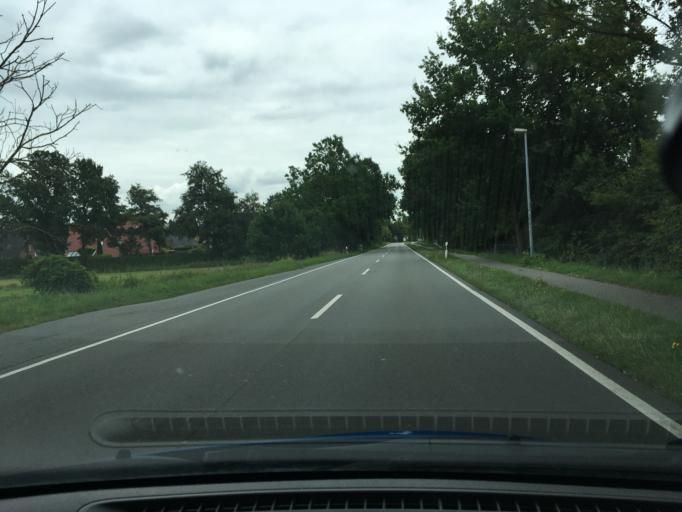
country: DE
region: Schleswig-Holstein
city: Lauenburg
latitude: 53.3619
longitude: 10.5573
